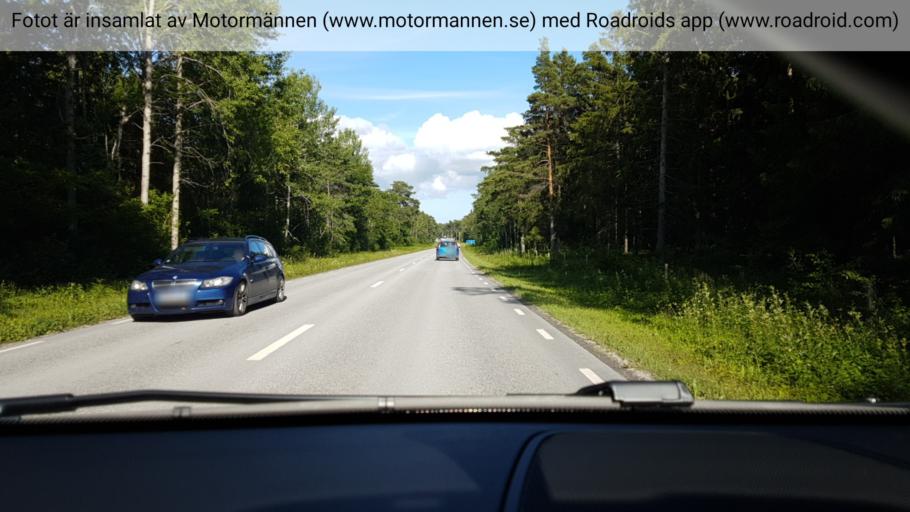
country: SE
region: Gotland
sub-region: Gotland
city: Slite
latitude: 57.7497
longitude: 18.7194
